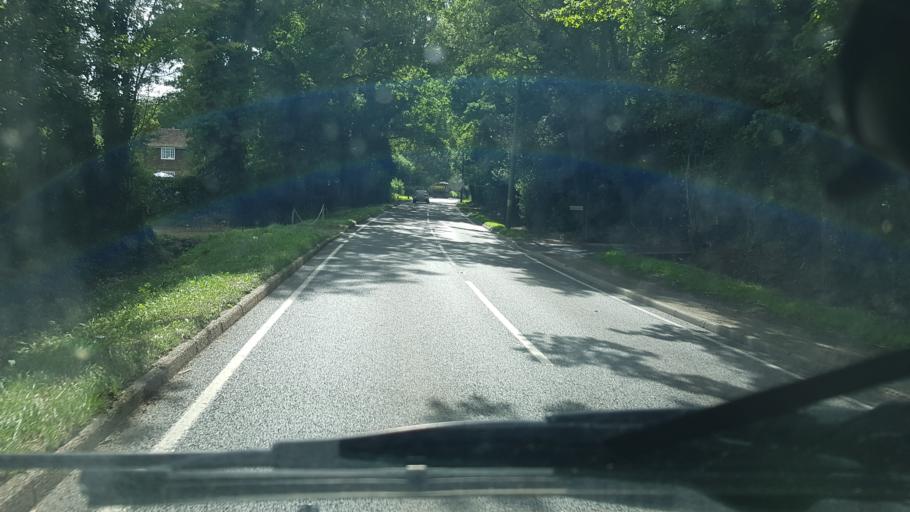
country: GB
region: England
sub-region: Surrey
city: Cranleigh
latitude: 51.1035
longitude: -0.5076
